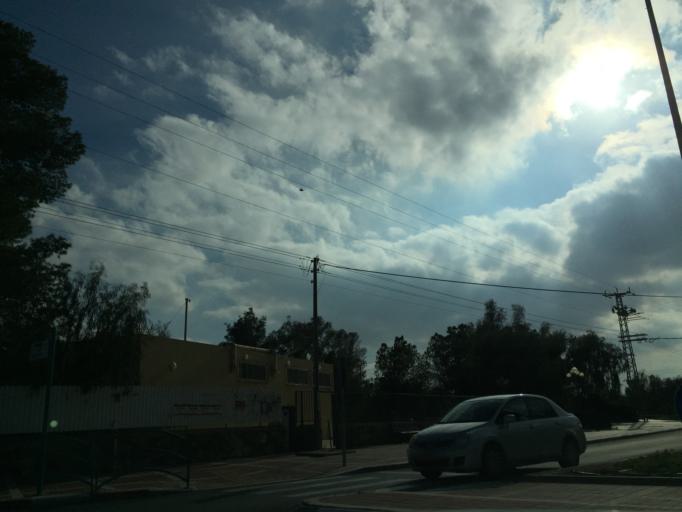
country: IL
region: Southern District
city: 'Arad
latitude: 31.2590
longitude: 35.2153
